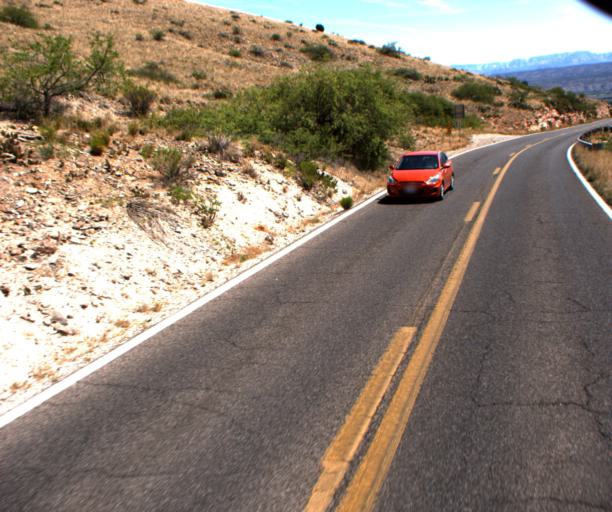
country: US
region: Arizona
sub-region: Yavapai County
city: Clarkdale
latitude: 34.7531
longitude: -112.0951
